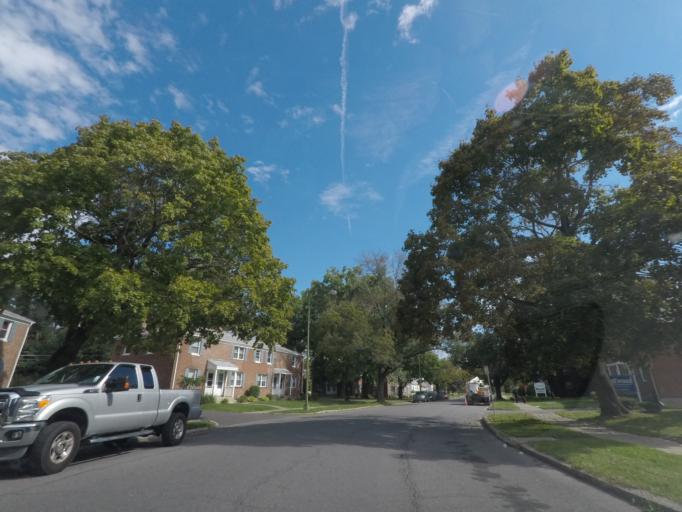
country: US
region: New York
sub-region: Albany County
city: Delmar
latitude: 42.6540
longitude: -73.8098
